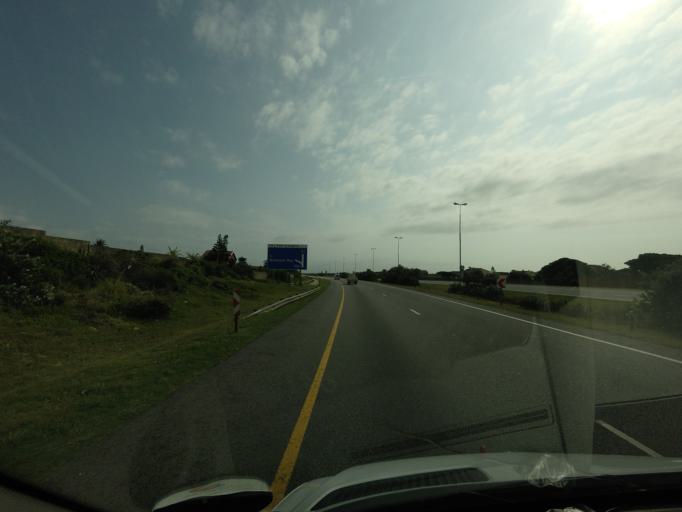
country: ZA
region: Eastern Cape
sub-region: Nelson Mandela Bay Metropolitan Municipality
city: Port Elizabeth
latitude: -33.8614
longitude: 25.6297
